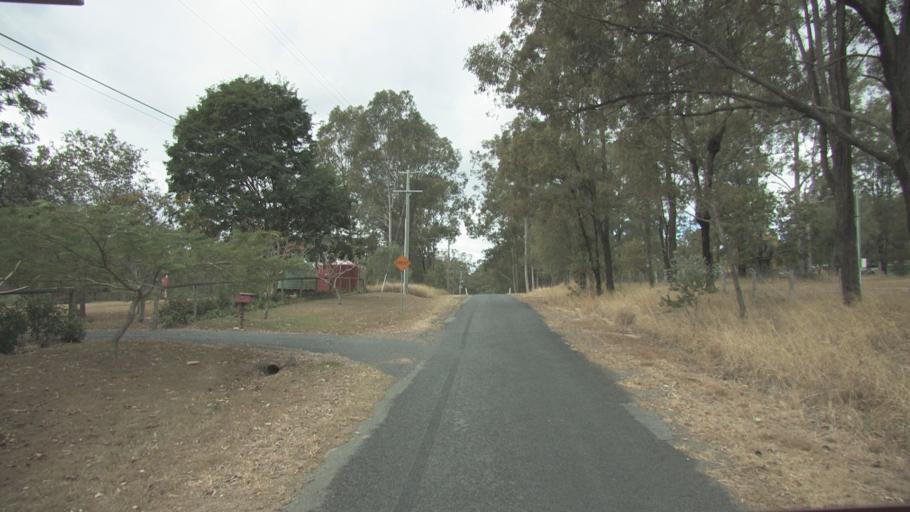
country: AU
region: Queensland
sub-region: Logan
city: Cedar Vale
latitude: -27.8828
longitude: 153.0306
